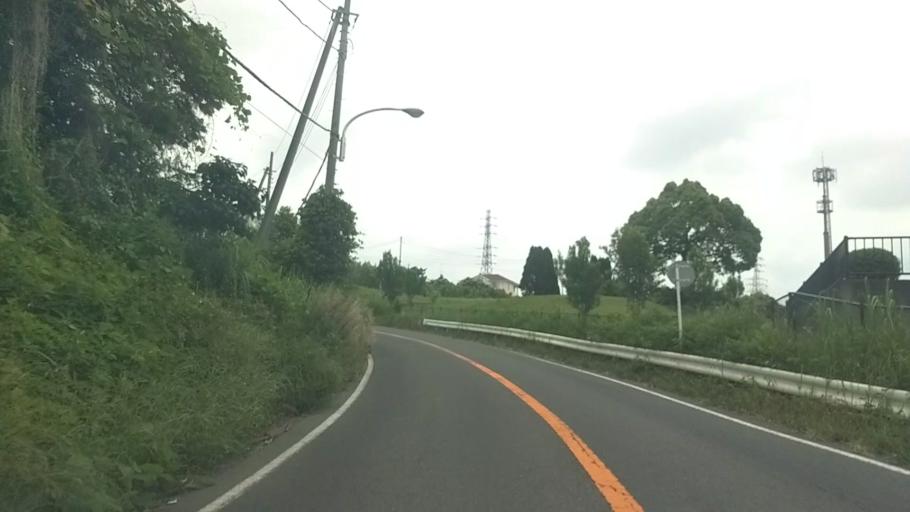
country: JP
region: Kanagawa
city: Fujisawa
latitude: 35.3598
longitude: 139.4356
